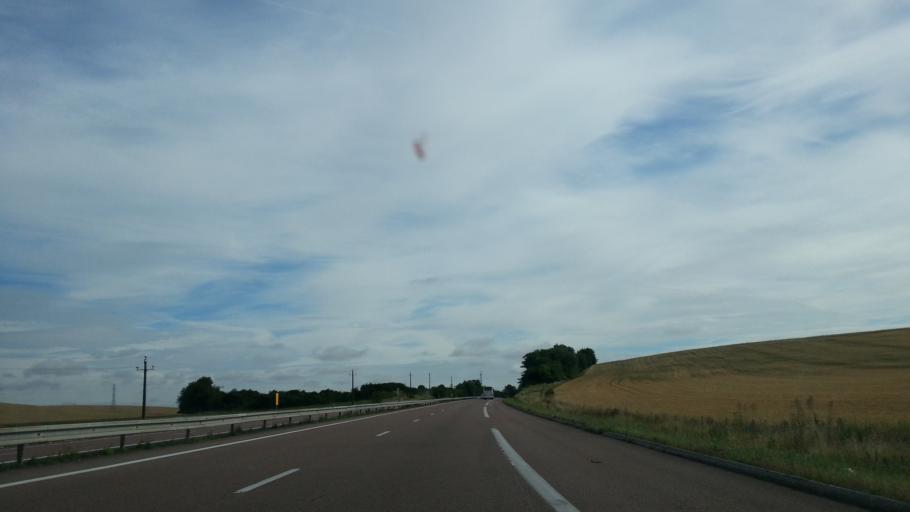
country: FR
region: Champagne-Ardenne
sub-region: Departement de la Marne
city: Chatillon-sur-Marne
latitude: 49.1919
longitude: 3.7550
